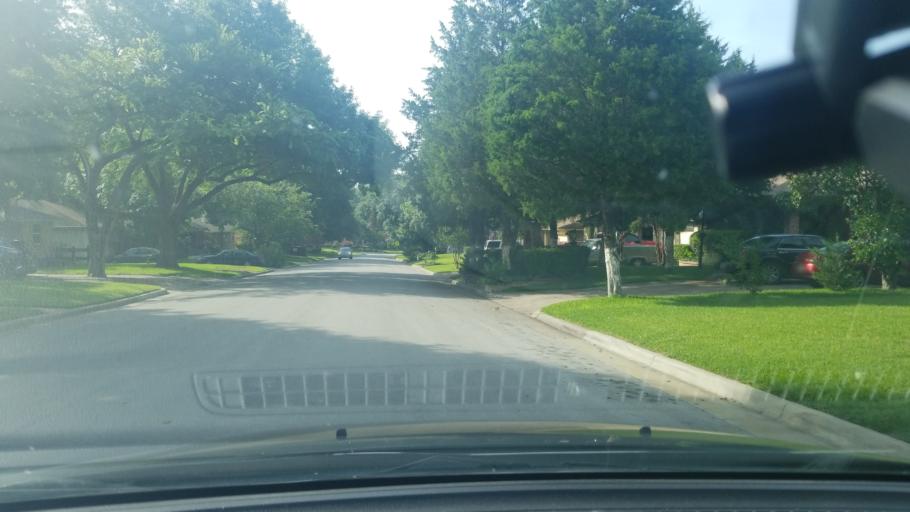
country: US
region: Texas
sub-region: Dallas County
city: Highland Park
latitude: 32.8037
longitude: -96.7099
